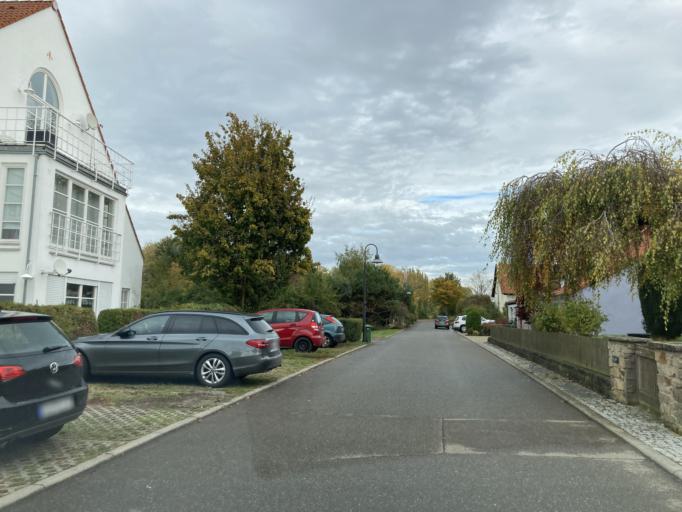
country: DE
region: Baden-Wuerttemberg
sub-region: Regierungsbezirk Stuttgart
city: Bondorf
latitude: 48.5067
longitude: 8.8825
